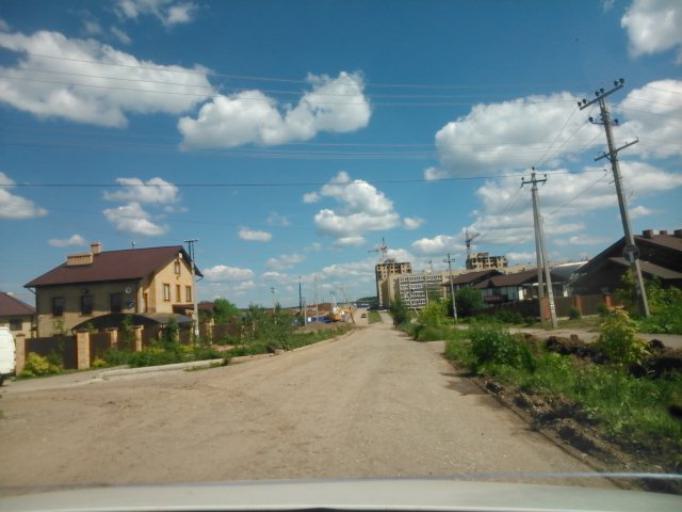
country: RU
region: Perm
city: Perm
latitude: 58.0027
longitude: 56.3318
